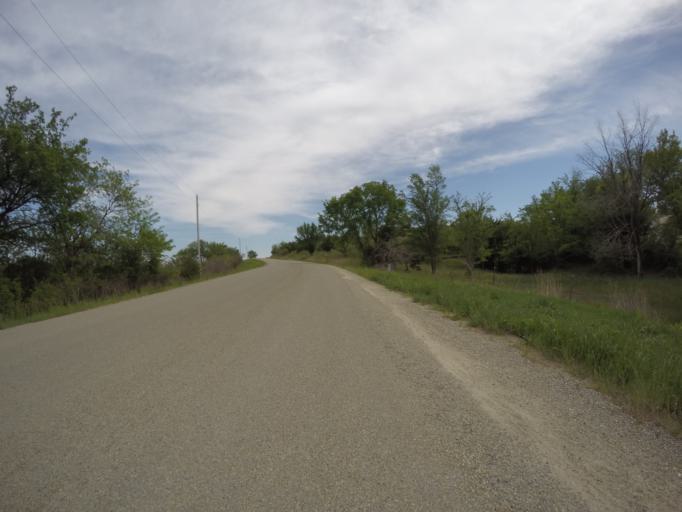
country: US
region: Kansas
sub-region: Riley County
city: Ogden
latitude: 39.0593
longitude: -96.6511
